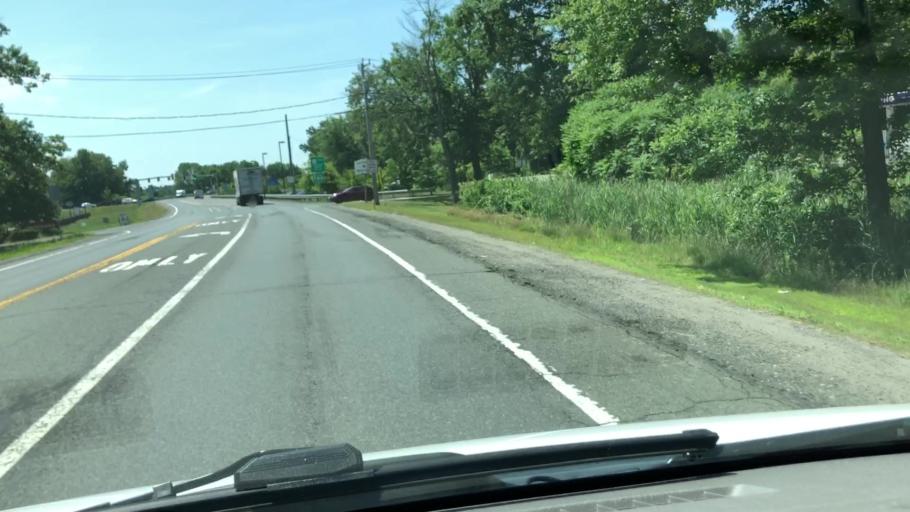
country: US
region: Massachusetts
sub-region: Franklin County
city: South Deerfield
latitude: 42.4714
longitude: -72.6147
